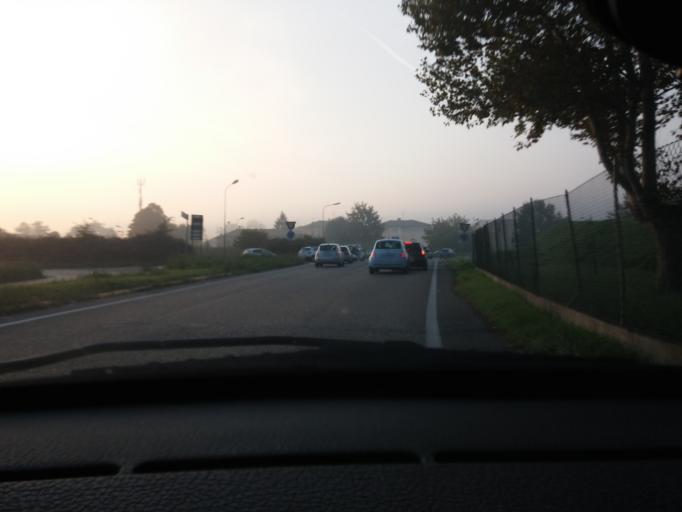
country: IT
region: Emilia-Romagna
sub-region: Provincia di Ferrara
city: Ferrara
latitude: 44.8353
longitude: 11.6006
